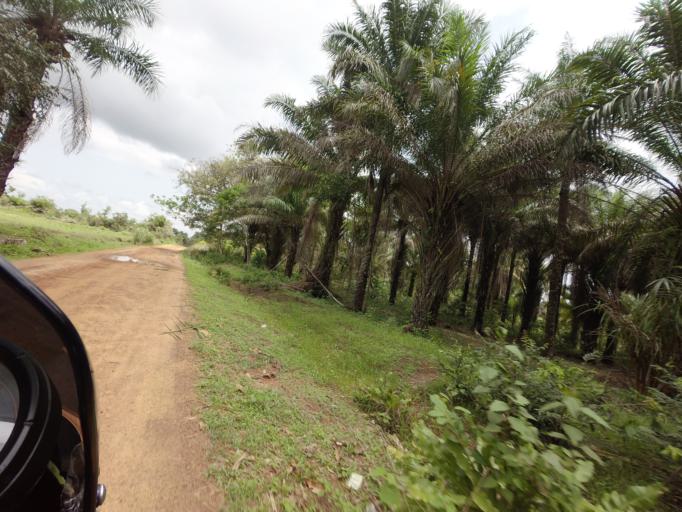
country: SL
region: Northern Province
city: Mambolo
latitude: 9.0044
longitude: -13.0127
